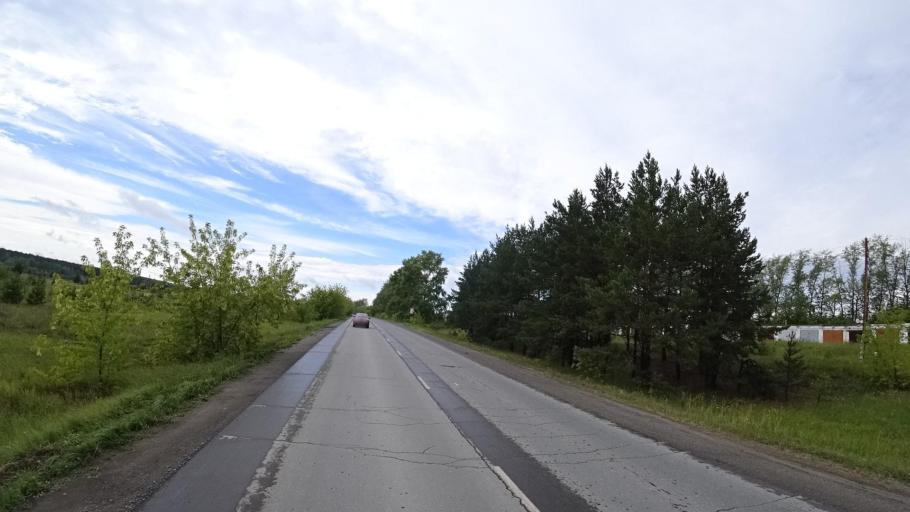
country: RU
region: Sverdlovsk
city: Kamyshlov
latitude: 56.8440
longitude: 62.7714
